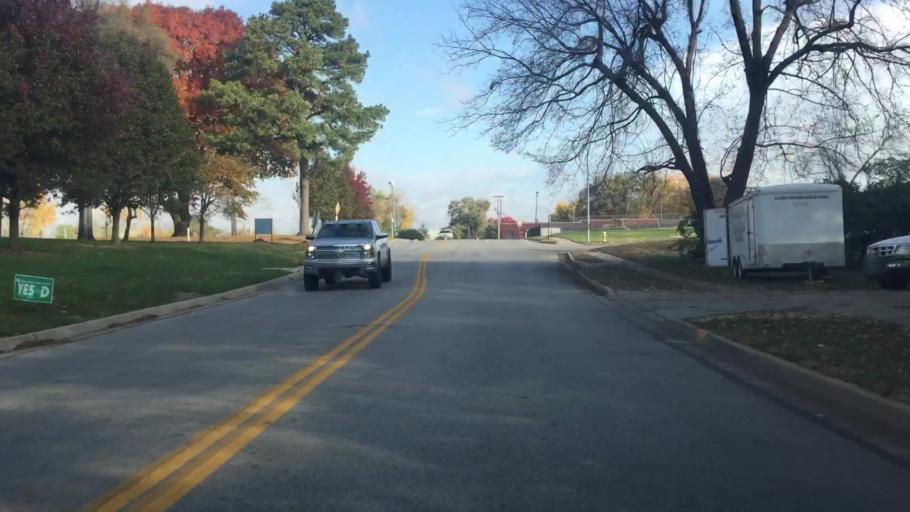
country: US
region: Missouri
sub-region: Jackson County
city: Grandview
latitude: 38.8881
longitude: -94.5396
